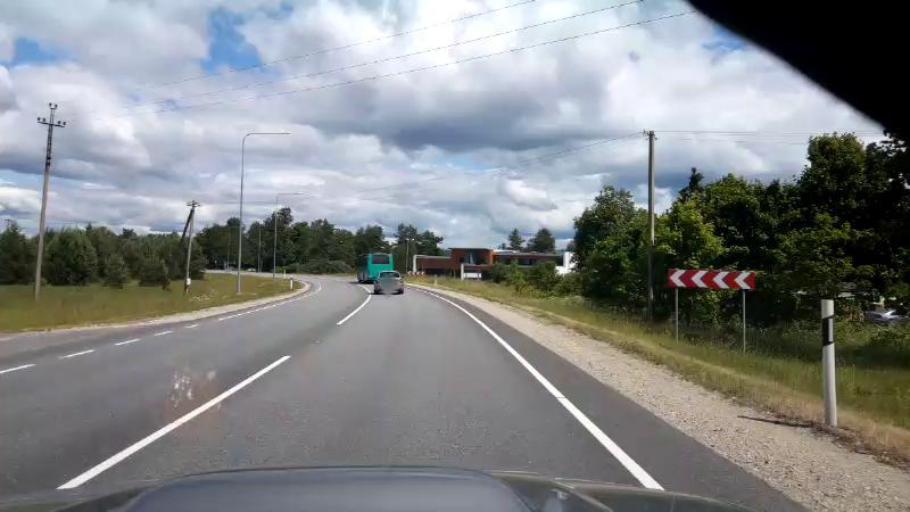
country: EE
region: Paernumaa
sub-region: Paikuse vald
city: Paikuse
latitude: 58.2967
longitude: 24.6080
